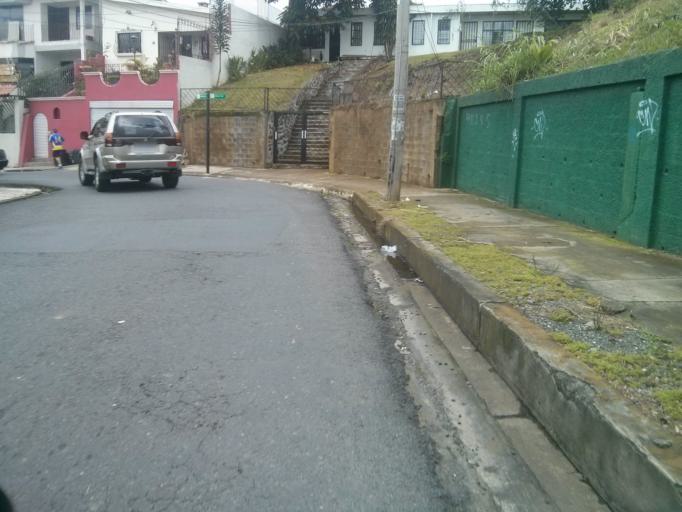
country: CR
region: San Jose
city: San Pedro
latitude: 9.9247
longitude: -84.0534
